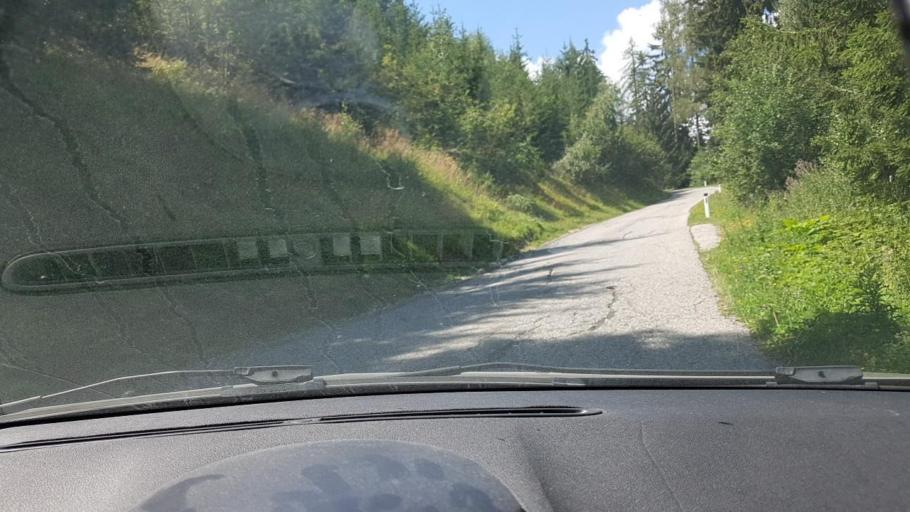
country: AT
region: Carinthia
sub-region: Politischer Bezirk Volkermarkt
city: Bad Eisenkappel
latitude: 46.4247
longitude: 14.5760
